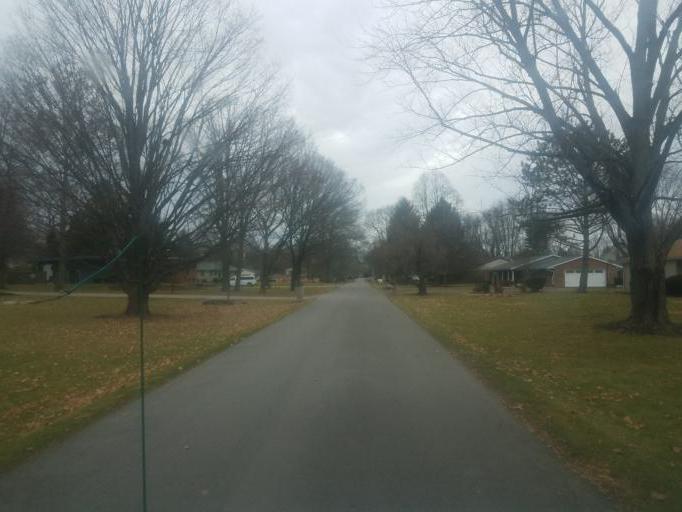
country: US
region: Ohio
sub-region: Marion County
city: Marion
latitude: 40.5659
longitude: -83.0814
